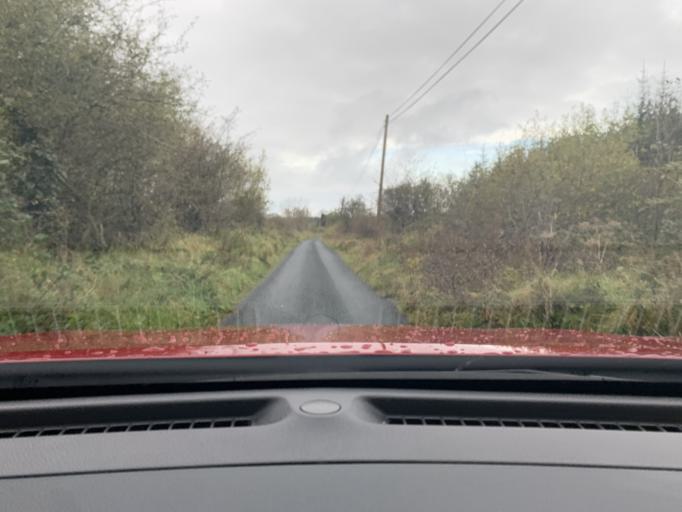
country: IE
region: Connaught
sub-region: Roscommon
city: Ballaghaderreen
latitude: 53.9740
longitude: -8.6055
